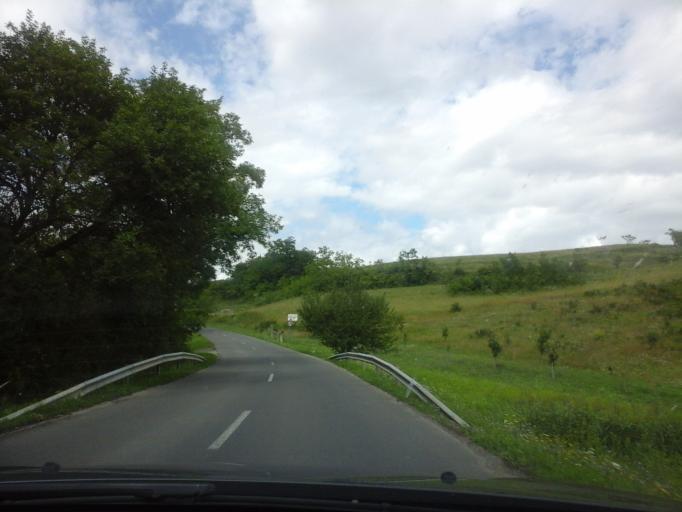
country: HU
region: Borsod-Abauj-Zemplen
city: Putnok
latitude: 48.4297
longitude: 20.4930
